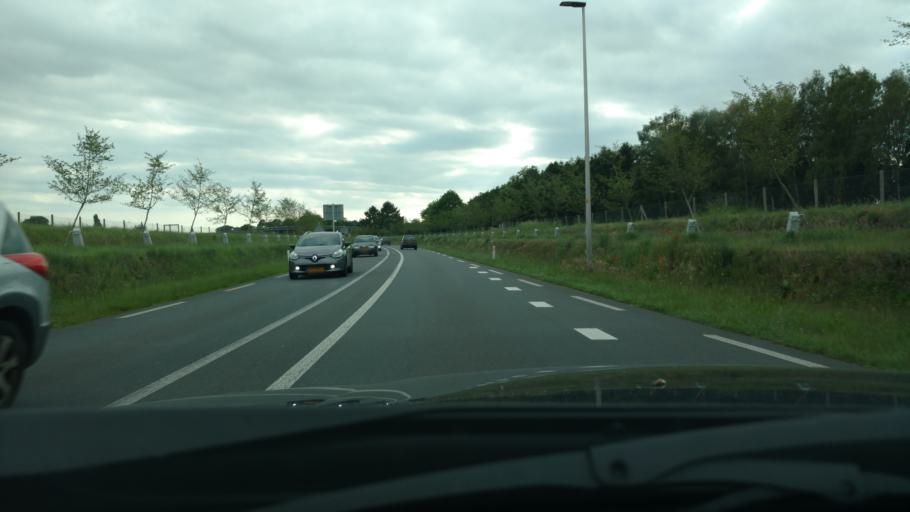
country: NL
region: Gelderland
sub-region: Gemeente Lochem
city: Eefde
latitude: 52.1757
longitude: 6.2182
